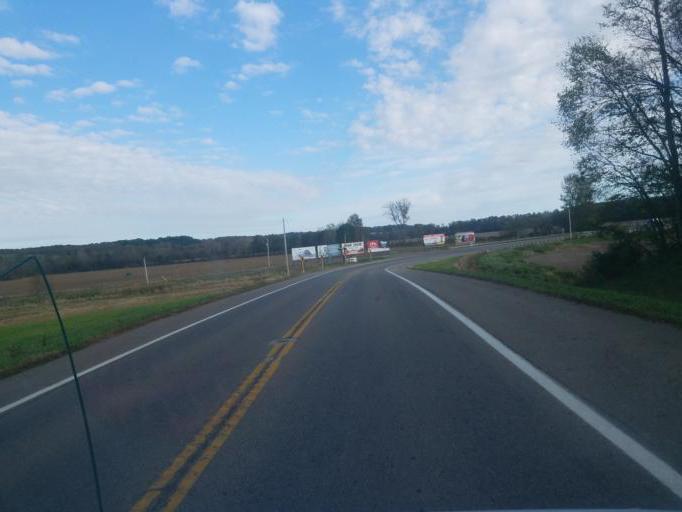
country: US
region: Ohio
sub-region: Holmes County
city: Millersburg
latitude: 40.6369
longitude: -81.9257
